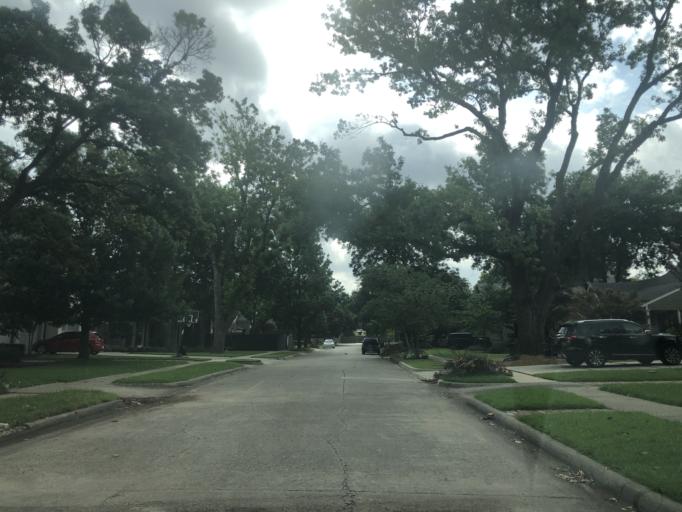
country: US
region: Texas
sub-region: Dallas County
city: University Park
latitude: 32.8542
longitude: -96.8249
